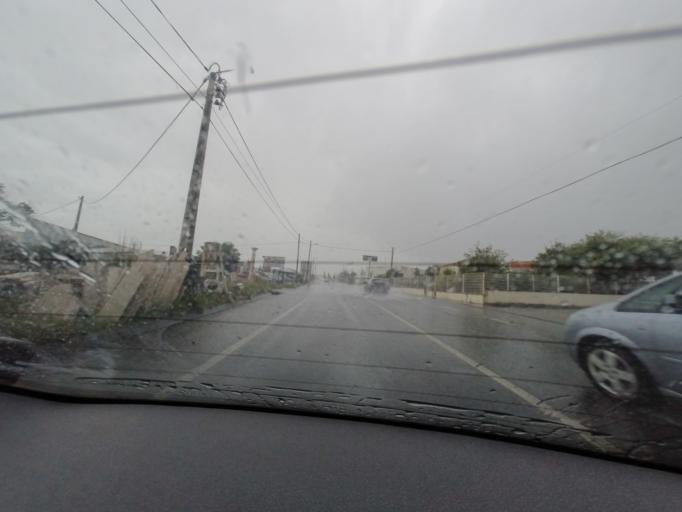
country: PT
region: Lisbon
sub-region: Sintra
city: Pero Pinheiro
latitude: 38.8364
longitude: -9.3558
